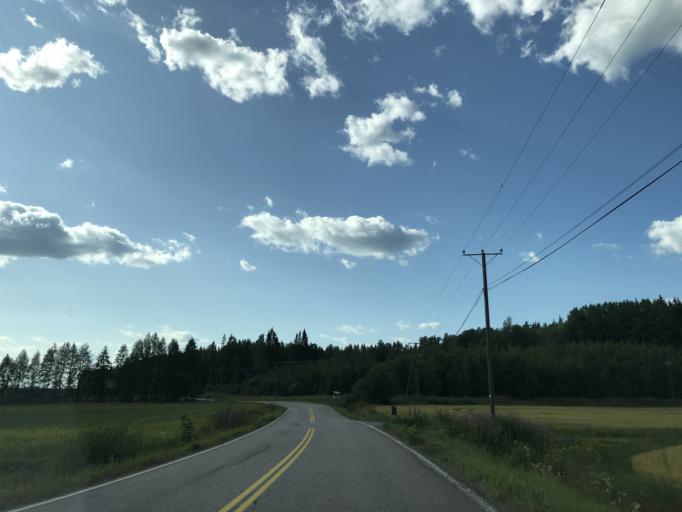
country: FI
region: Uusimaa
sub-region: Helsinki
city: Nurmijaervi
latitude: 60.4507
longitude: 24.6413
